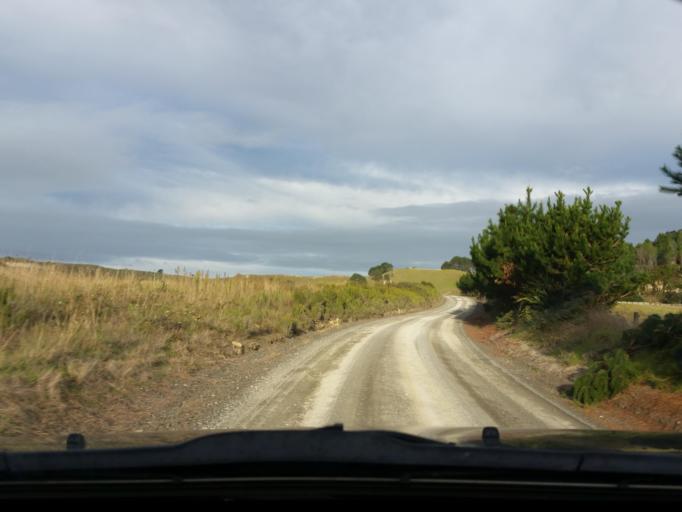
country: NZ
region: Northland
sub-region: Kaipara District
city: Dargaville
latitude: -35.9013
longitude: 173.7318
